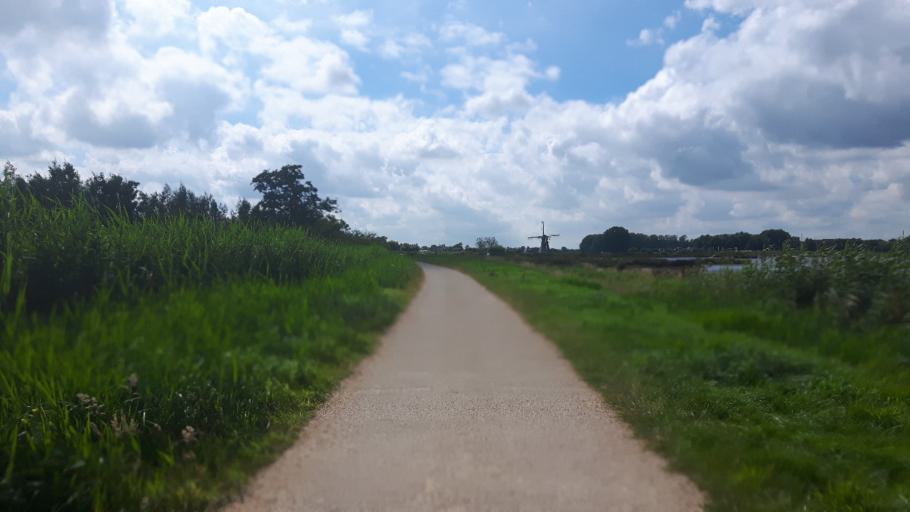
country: NL
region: South Holland
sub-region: Gemeente Vlist
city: Haastrecht
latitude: 51.9921
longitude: 4.7937
